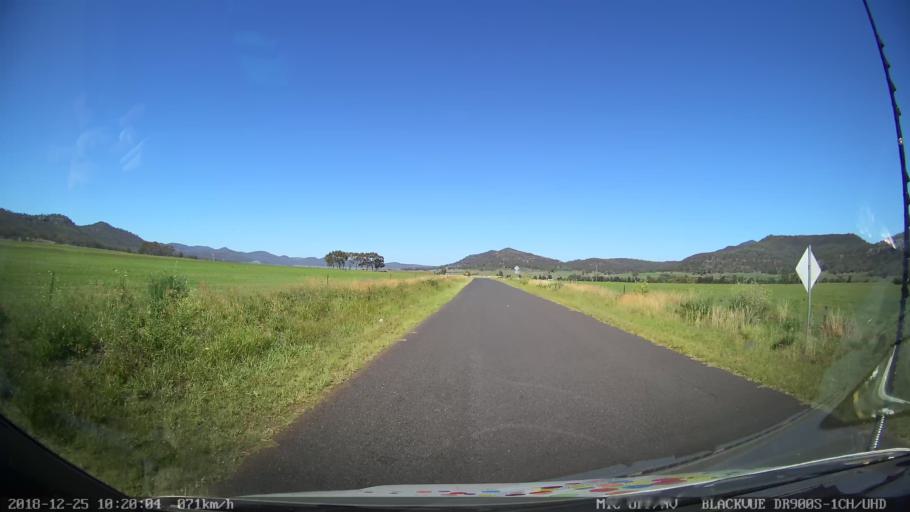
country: AU
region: New South Wales
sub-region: Muswellbrook
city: Denman
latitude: -32.3560
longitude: 150.5528
